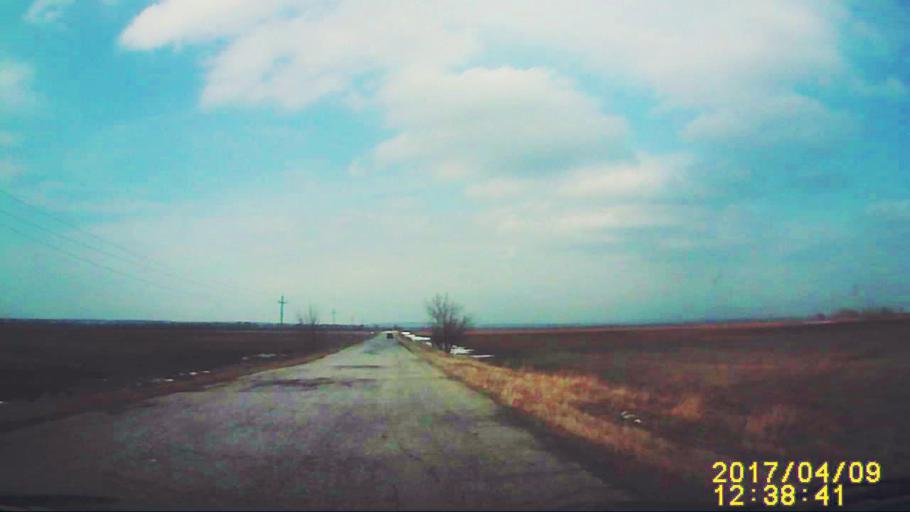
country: RU
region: Ulyanovsk
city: Ignatovka
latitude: 53.9960
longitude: 47.9641
